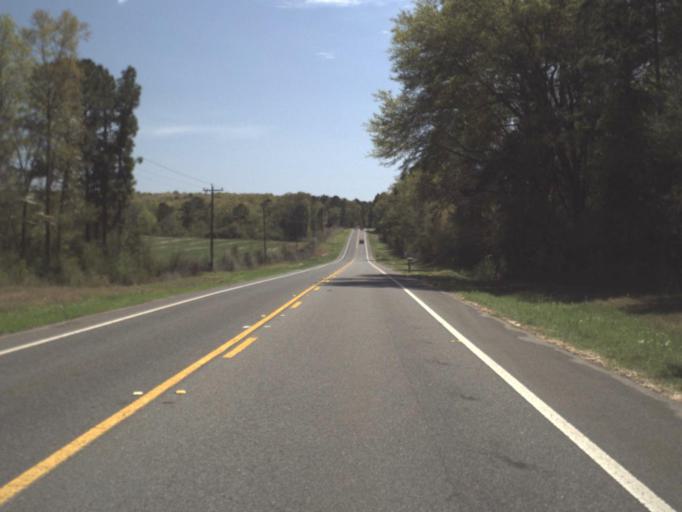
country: US
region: Alabama
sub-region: Geneva County
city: Geneva
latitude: 30.8688
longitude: -85.9458
